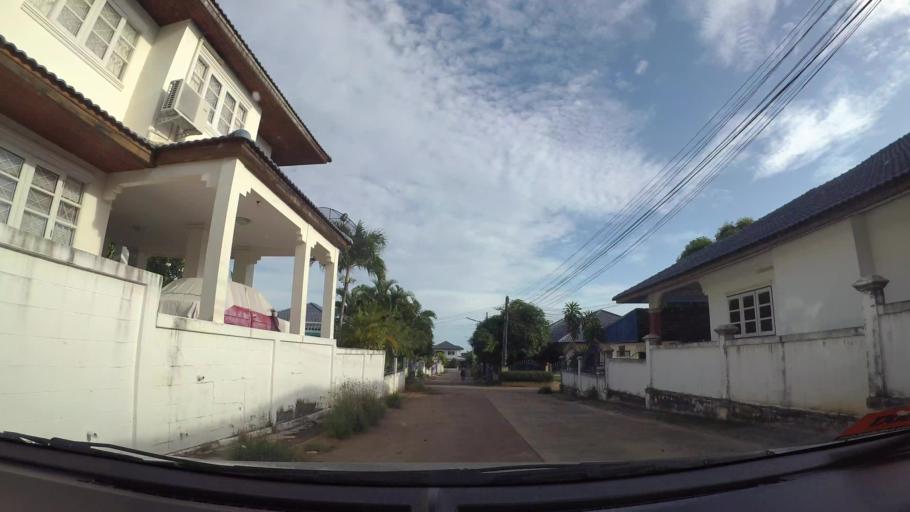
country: TH
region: Chon Buri
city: Sattahip
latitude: 12.6723
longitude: 100.9191
